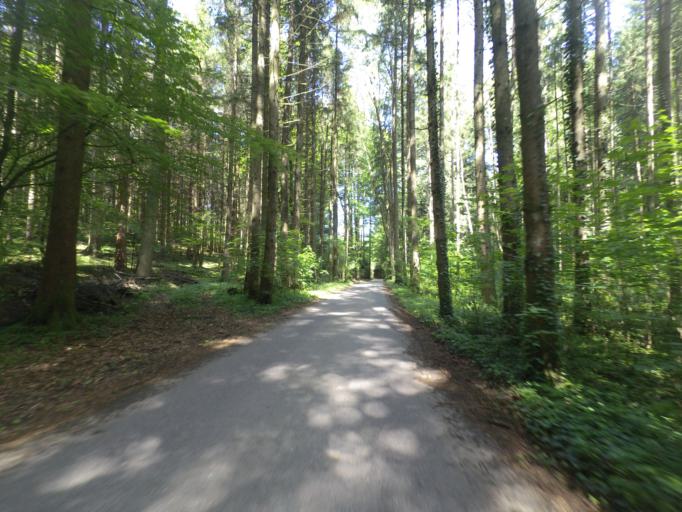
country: DE
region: Bavaria
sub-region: Upper Bavaria
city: Petting
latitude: 47.8985
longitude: 12.8137
